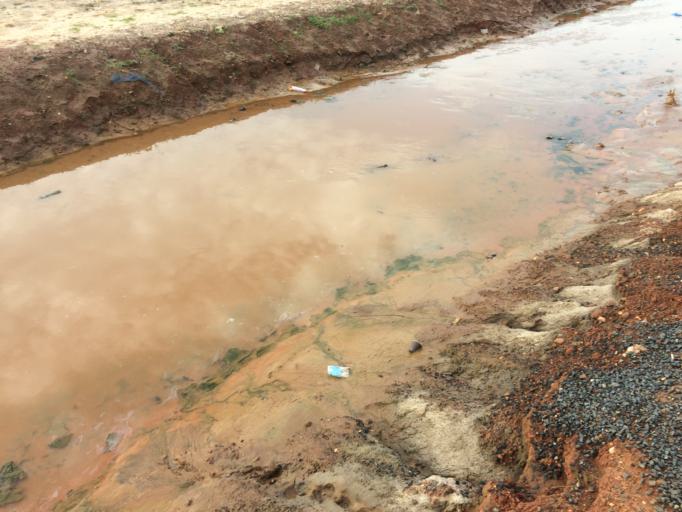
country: SN
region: Dakar
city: Pikine
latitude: 14.7407
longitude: -17.3083
